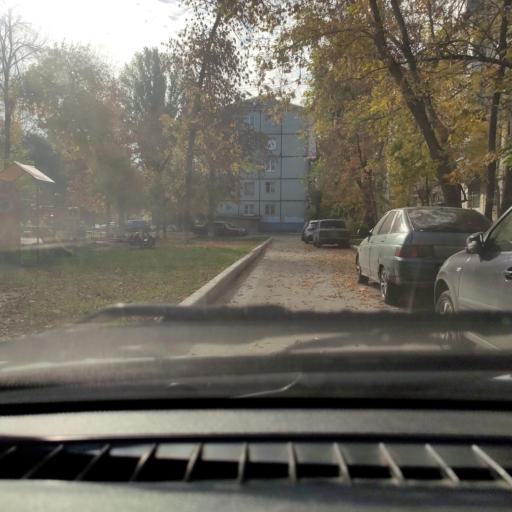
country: RU
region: Samara
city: Tol'yatti
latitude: 53.5016
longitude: 49.4067
